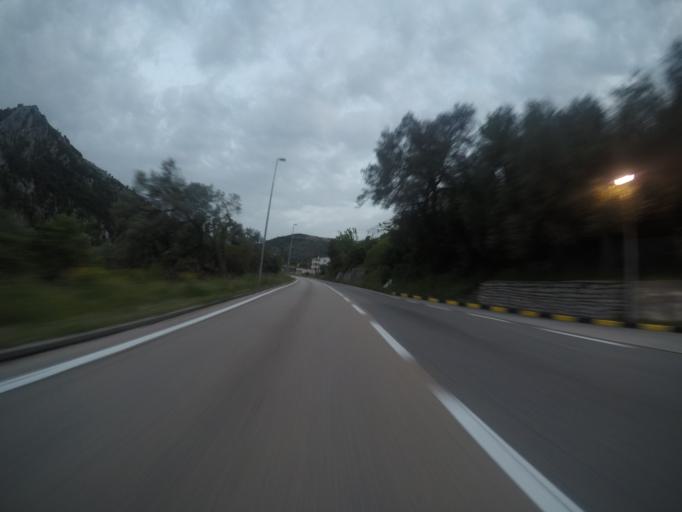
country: ME
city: Petrovac na Moru
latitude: 42.2007
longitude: 18.9634
